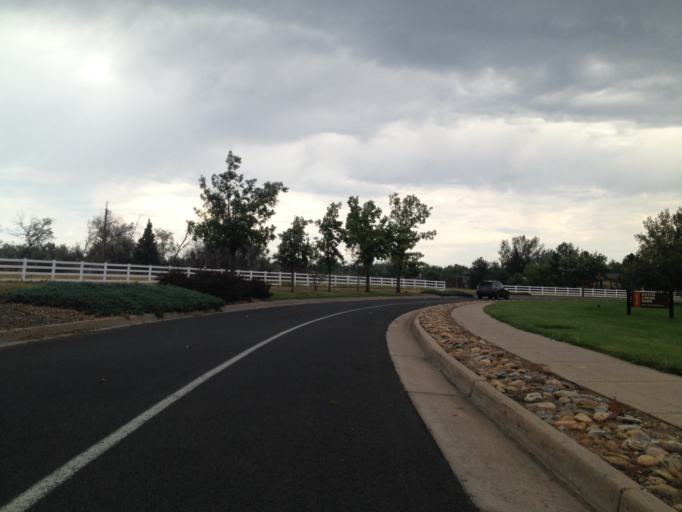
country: US
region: Colorado
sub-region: Boulder County
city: Louisville
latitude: 39.9681
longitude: -105.1421
